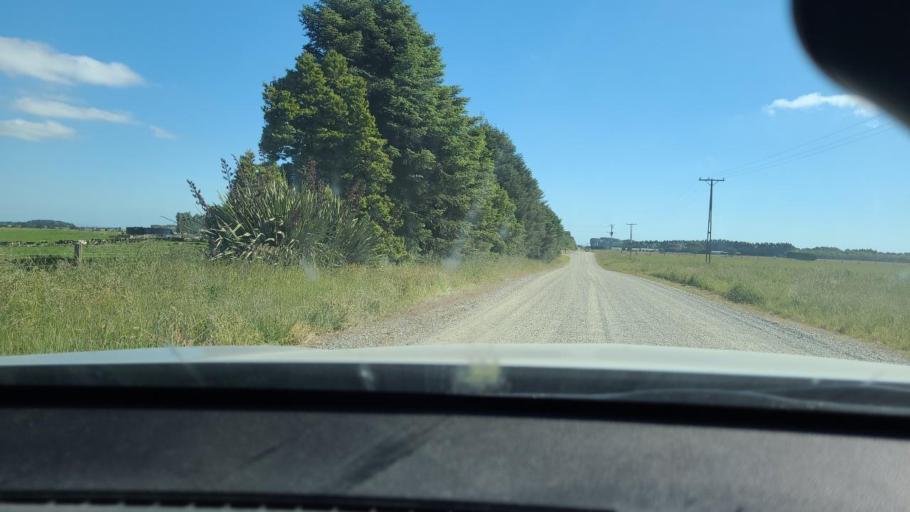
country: NZ
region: Southland
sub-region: Southland District
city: Winton
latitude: -46.2603
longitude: 168.2277
